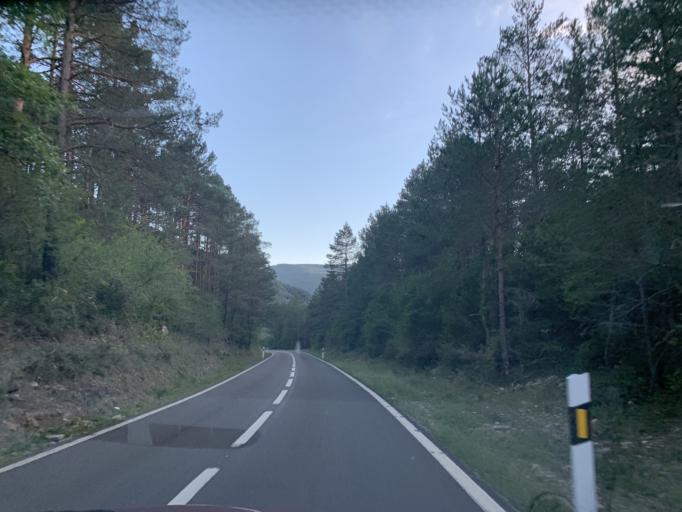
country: ES
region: Aragon
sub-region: Provincia de Huesca
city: Broto
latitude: 42.5562
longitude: -0.1210
